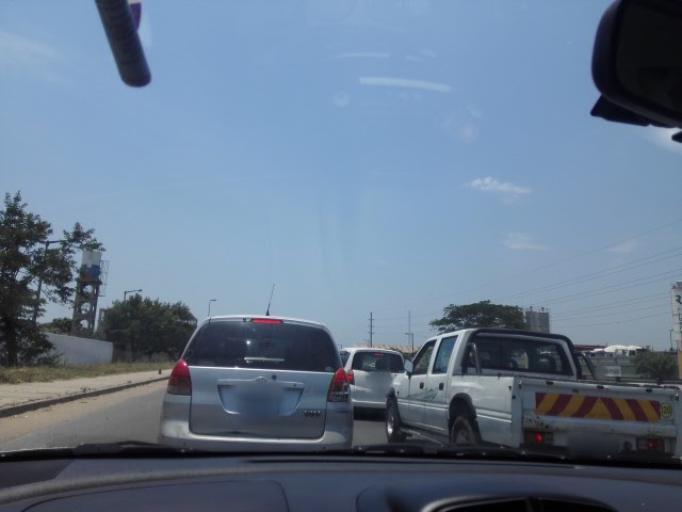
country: MZ
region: Maputo City
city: Maputo
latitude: -25.9397
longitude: 32.5688
